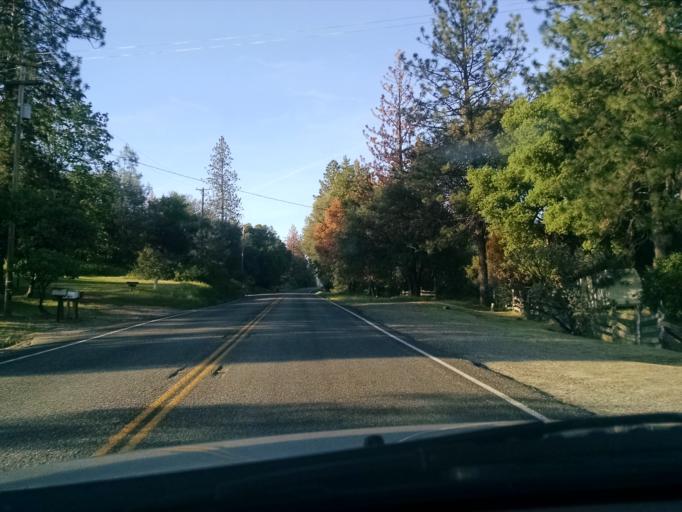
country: US
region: California
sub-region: Madera County
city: Ahwahnee
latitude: 37.4089
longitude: -119.7334
